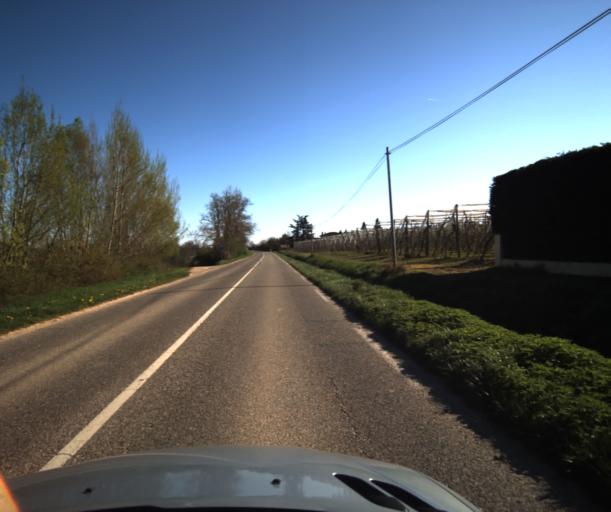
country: FR
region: Midi-Pyrenees
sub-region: Departement du Tarn-et-Garonne
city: Bressols
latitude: 43.9577
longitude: 1.3445
